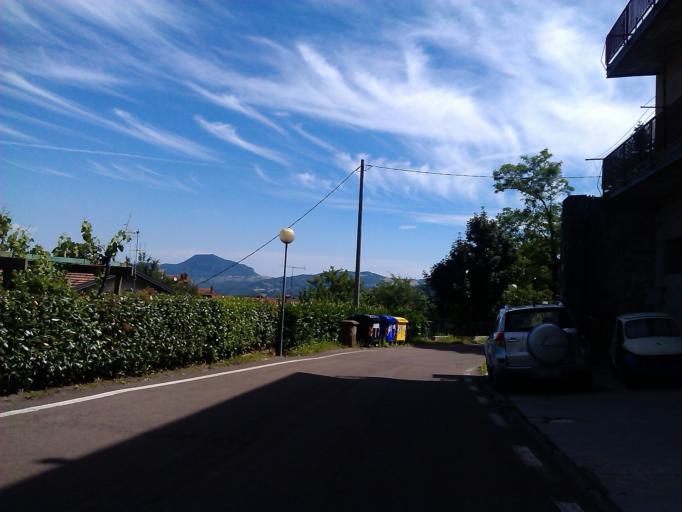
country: IT
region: Tuscany
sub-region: Provincia di Pistoia
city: Sambuca Pistoiese
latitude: 44.1173
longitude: 11.0306
